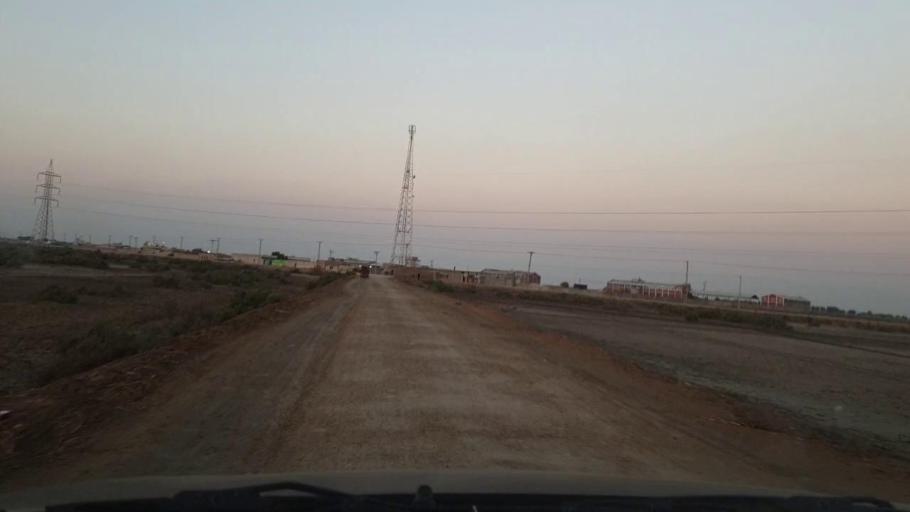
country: PK
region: Sindh
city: Jhol
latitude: 25.9509
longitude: 68.9762
